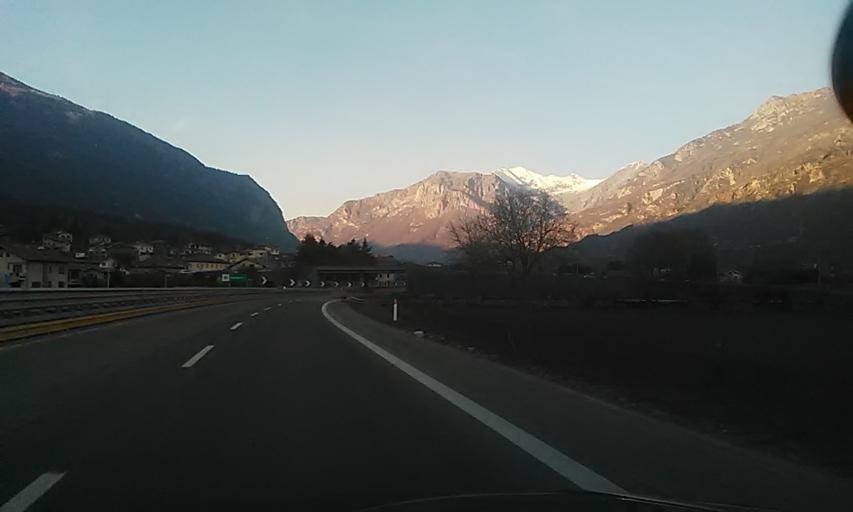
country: IT
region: Piedmont
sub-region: Provincia di Torino
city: Tavagnasco
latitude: 45.5429
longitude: 7.8255
